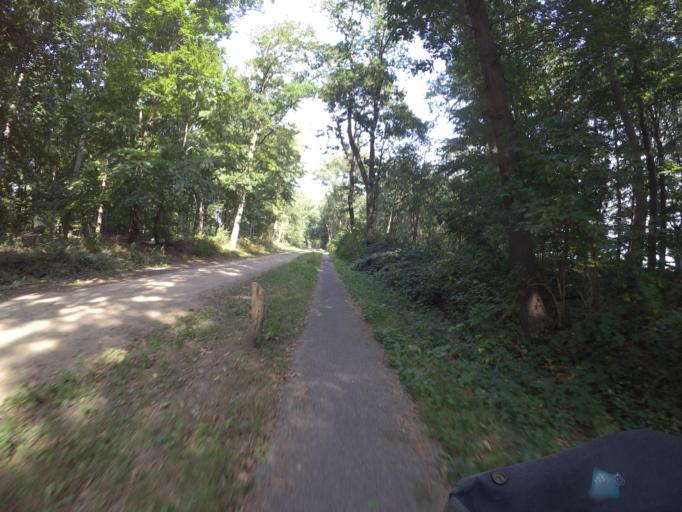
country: NL
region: Drenthe
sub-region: Gemeente Westerveld
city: Havelte
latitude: 52.7711
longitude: 6.2088
